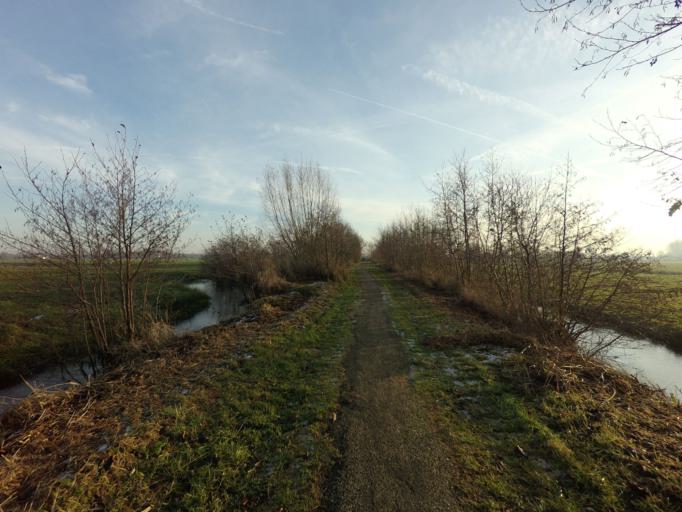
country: NL
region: Utrecht
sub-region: Stichtse Vecht
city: Breukelen
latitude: 52.1766
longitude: 4.9342
